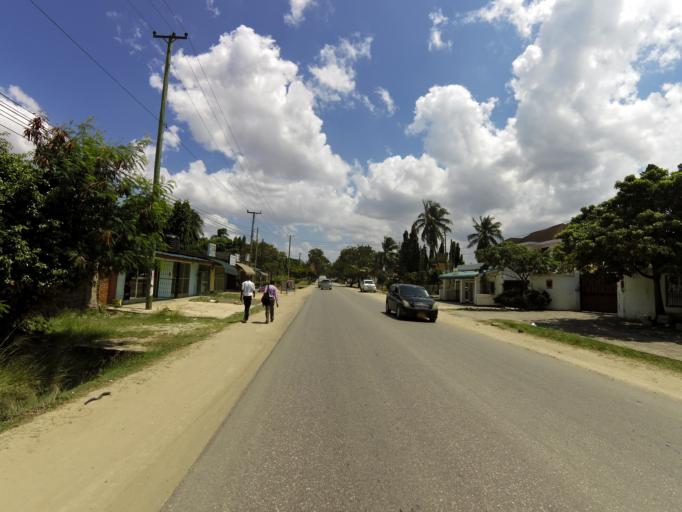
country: TZ
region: Dar es Salaam
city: Magomeni
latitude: -6.7640
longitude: 39.2494
